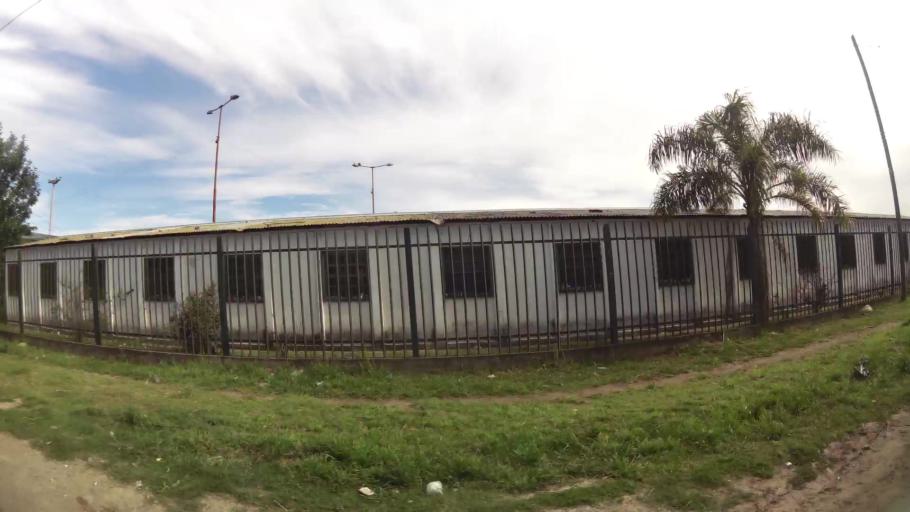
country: AR
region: Santa Fe
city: Granadero Baigorria
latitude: -32.9149
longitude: -60.7103
